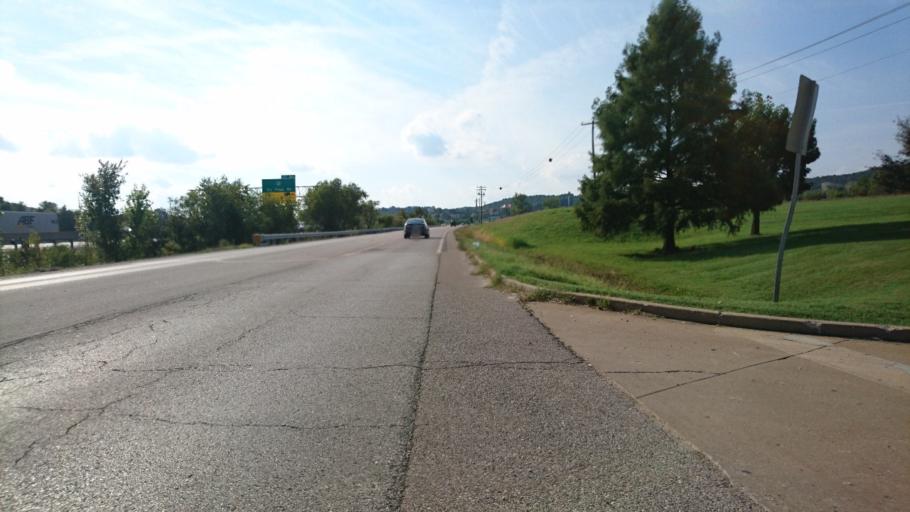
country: US
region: Missouri
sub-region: Saint Louis County
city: Eureka
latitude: 38.5051
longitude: -90.6688
